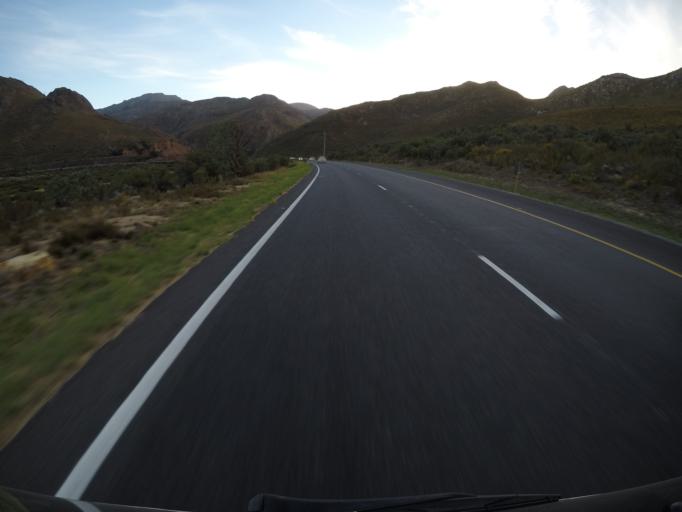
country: ZA
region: Western Cape
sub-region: Cape Winelands District Municipality
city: Paarl
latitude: -33.7272
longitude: 19.1220
